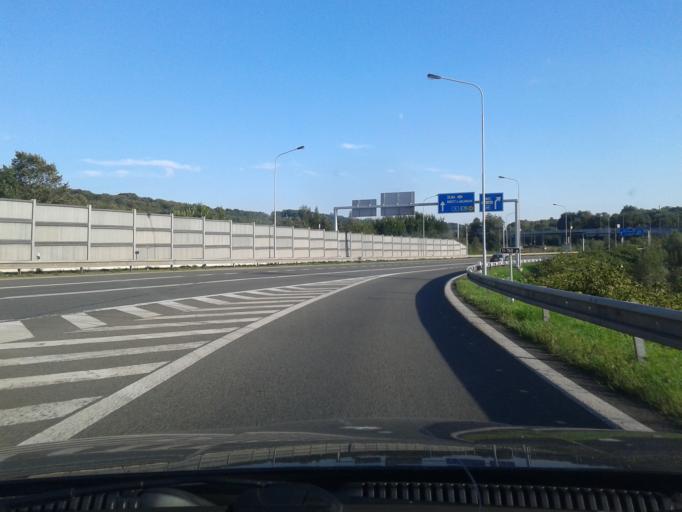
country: CZ
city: Ropice
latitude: 49.7218
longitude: 18.6197
